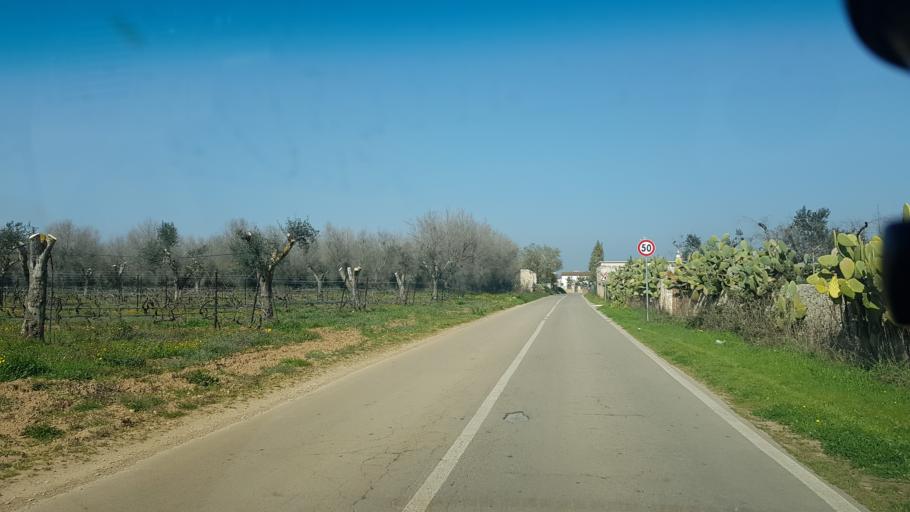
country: IT
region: Apulia
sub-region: Provincia di Lecce
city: Squinzano
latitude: 40.4491
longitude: 18.0412
